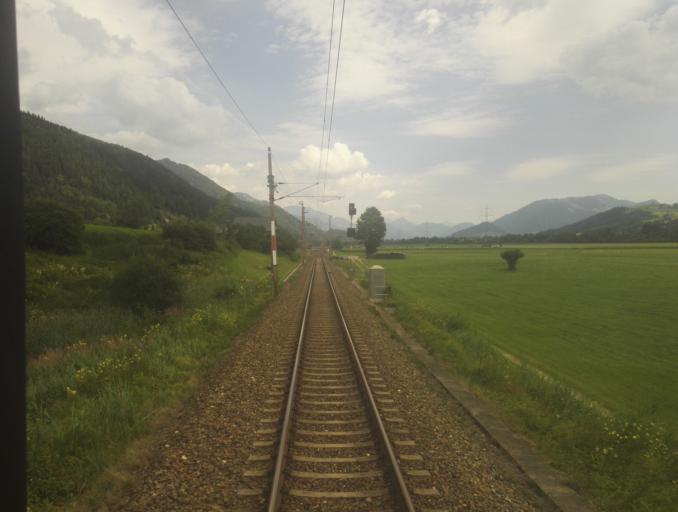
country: AT
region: Styria
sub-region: Politischer Bezirk Liezen
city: Niederoblarn
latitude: 47.4921
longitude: 14.0228
